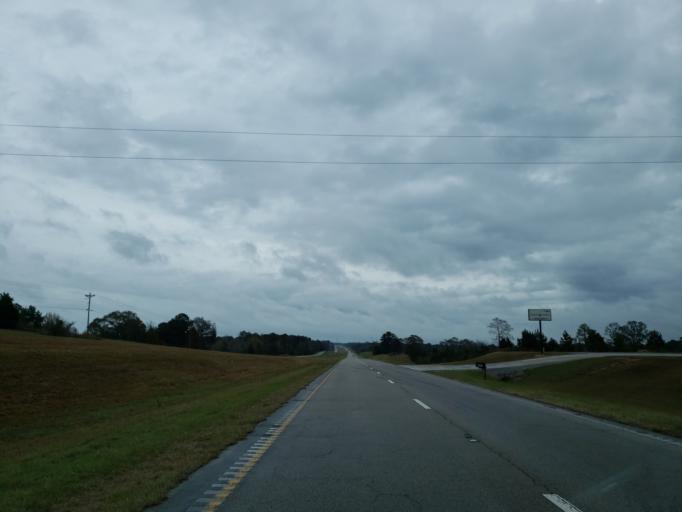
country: US
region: Mississippi
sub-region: Wayne County
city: Waynesboro
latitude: 31.6966
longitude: -88.8637
